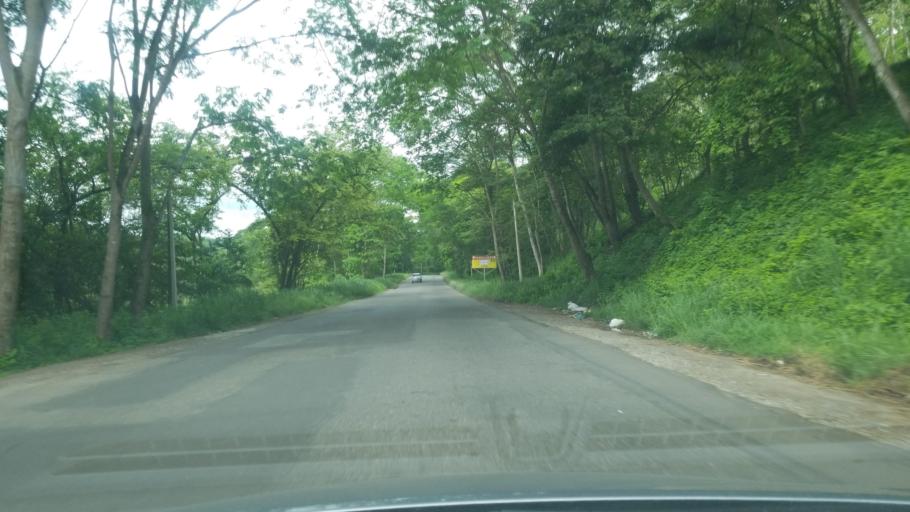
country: HN
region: Santa Barbara
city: Camalote
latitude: 15.3242
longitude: -88.3098
